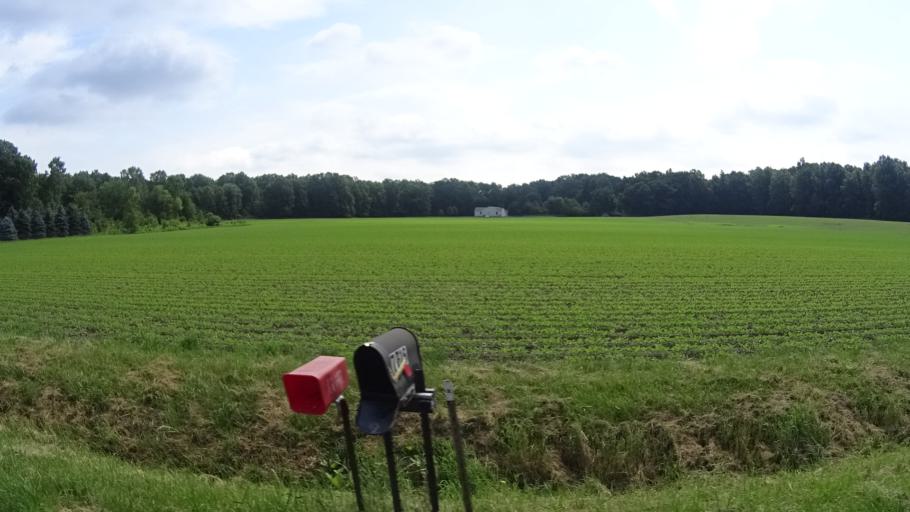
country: US
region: Ohio
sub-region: Lorain County
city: Vermilion
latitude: 41.3746
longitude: -82.4055
